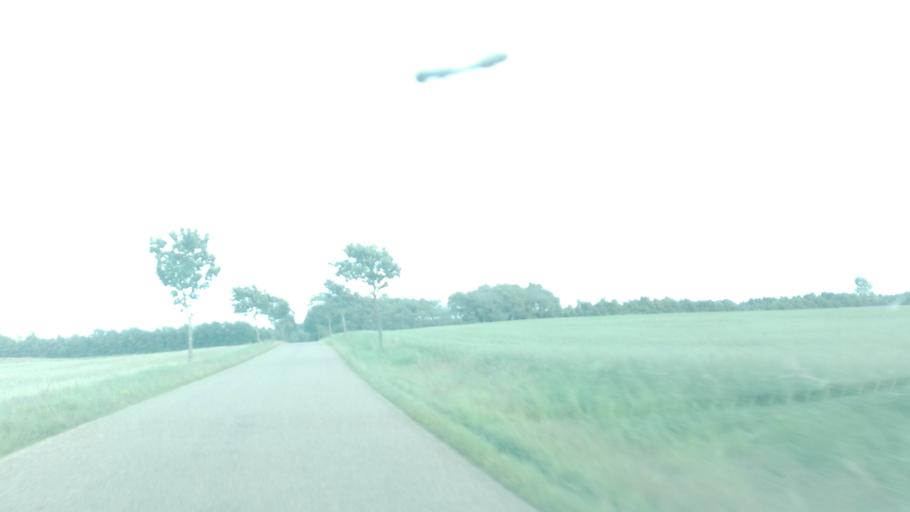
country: DK
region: Central Jutland
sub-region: Silkeborg Kommune
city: Virklund
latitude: 56.0846
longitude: 9.5817
